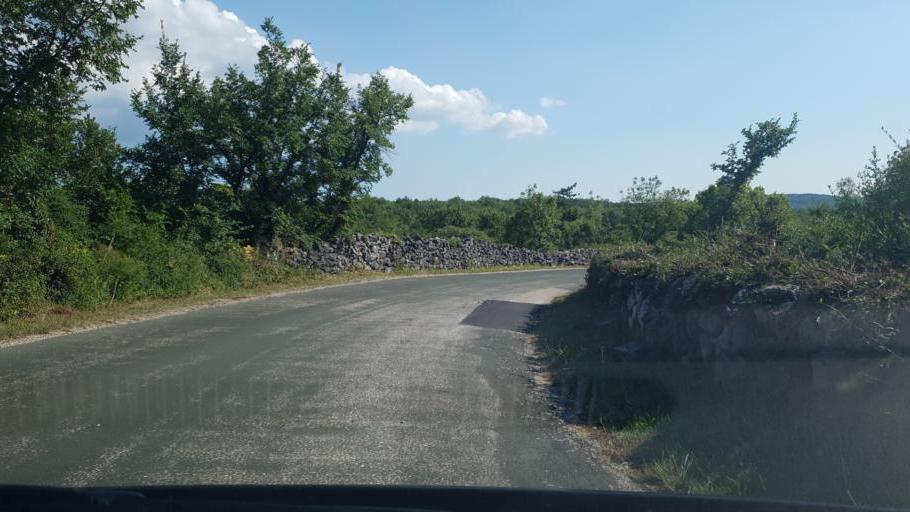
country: HR
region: Primorsko-Goranska
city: Omisalj
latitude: 45.1791
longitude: 14.5944
